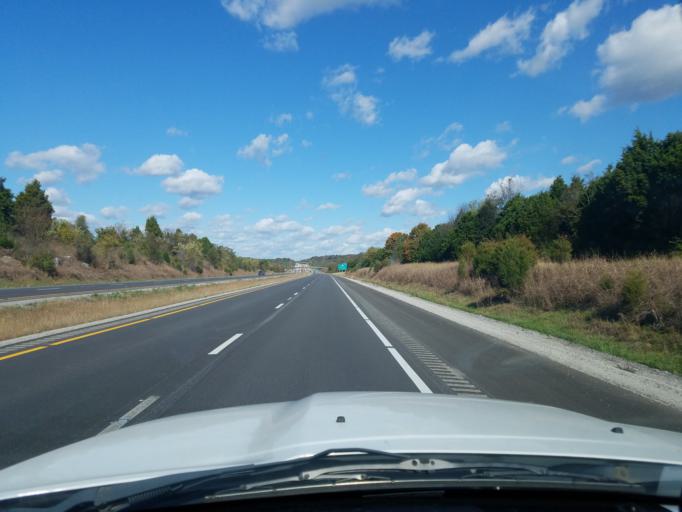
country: US
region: Kentucky
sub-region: Warren County
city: Bowling Green
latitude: 36.9835
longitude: -86.5019
